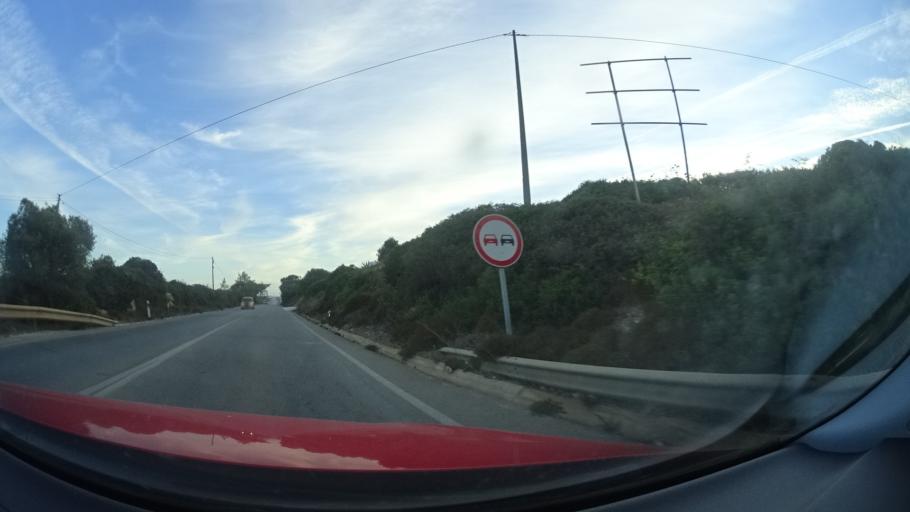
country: PT
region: Faro
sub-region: Vila do Bispo
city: Sagres
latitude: 37.0220
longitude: -8.9383
